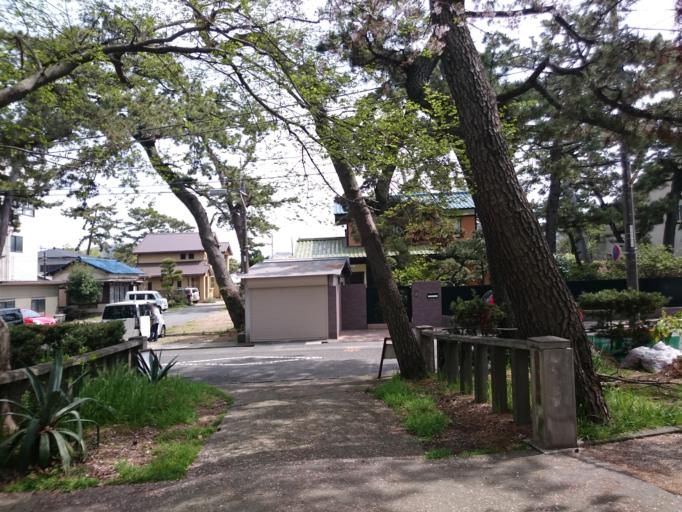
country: JP
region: Shizuoka
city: Numazu
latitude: 35.0832
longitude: 138.8548
